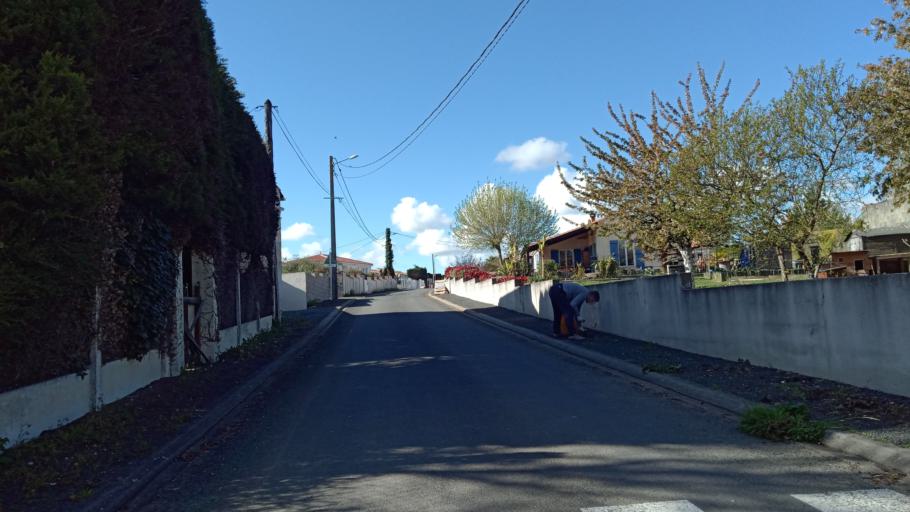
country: FR
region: Poitou-Charentes
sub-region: Departement de la Charente-Maritime
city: Verines
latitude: 46.1540
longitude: -0.9328
